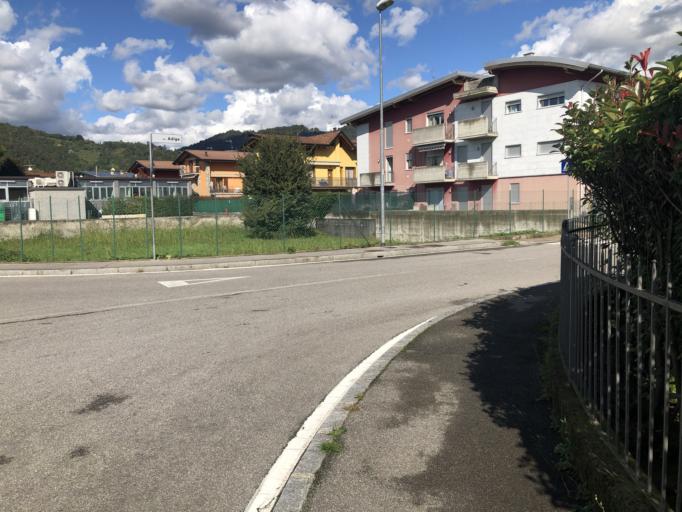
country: IT
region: Lombardy
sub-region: Provincia di Bergamo
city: Negrone
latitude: 45.7066
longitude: 9.7576
